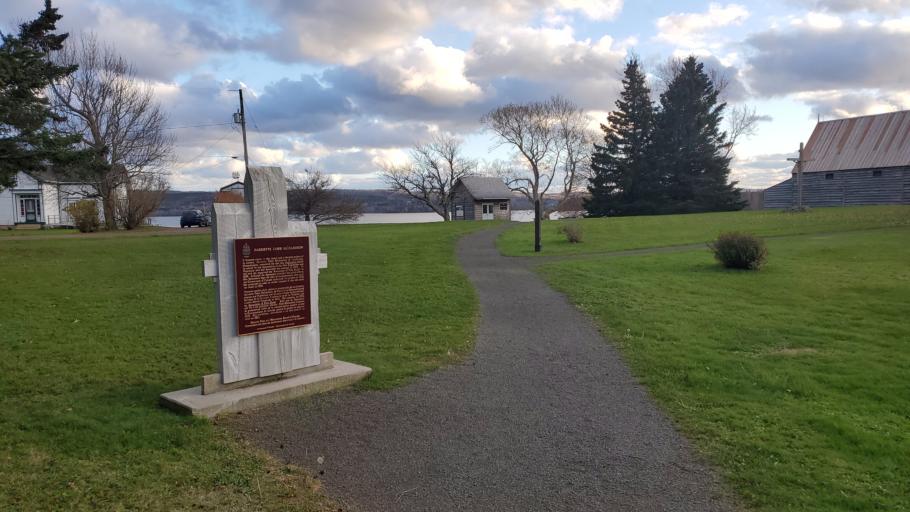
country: CA
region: Nova Scotia
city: Digby
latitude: 44.7121
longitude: -65.6093
